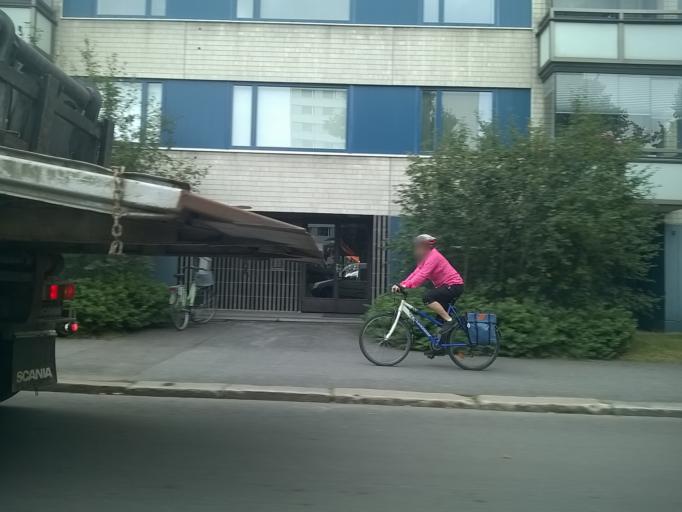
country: FI
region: Pirkanmaa
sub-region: Tampere
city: Tampere
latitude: 61.5025
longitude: 23.7508
